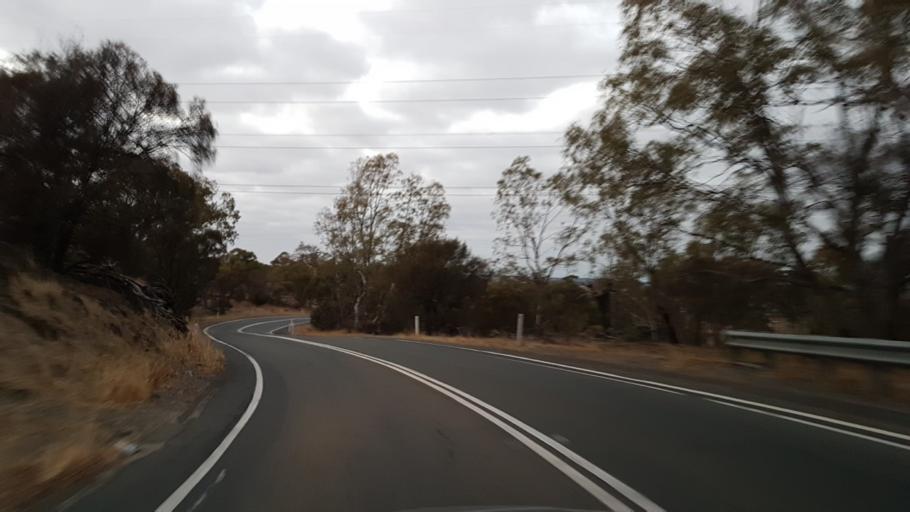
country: AU
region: South Australia
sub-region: Mount Barker
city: Callington
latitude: -35.0478
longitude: 138.9988
